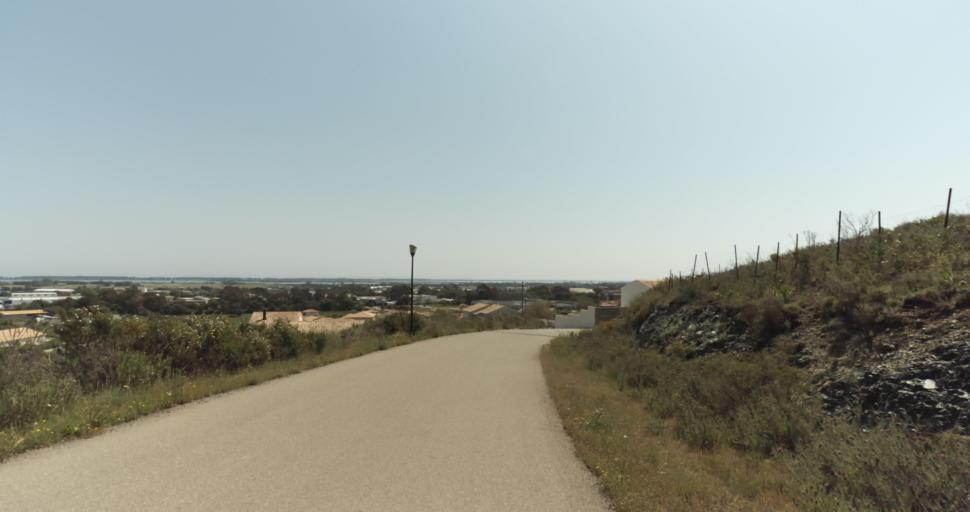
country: FR
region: Corsica
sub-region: Departement de la Haute-Corse
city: Biguglia
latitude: 42.6015
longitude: 9.4295
